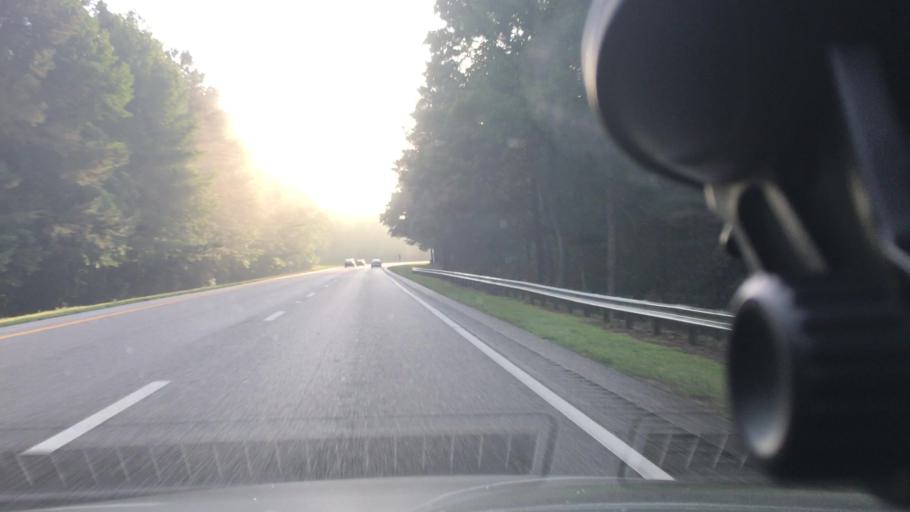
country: US
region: North Carolina
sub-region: Wake County
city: Zebulon
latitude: 35.7948
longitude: -78.1599
